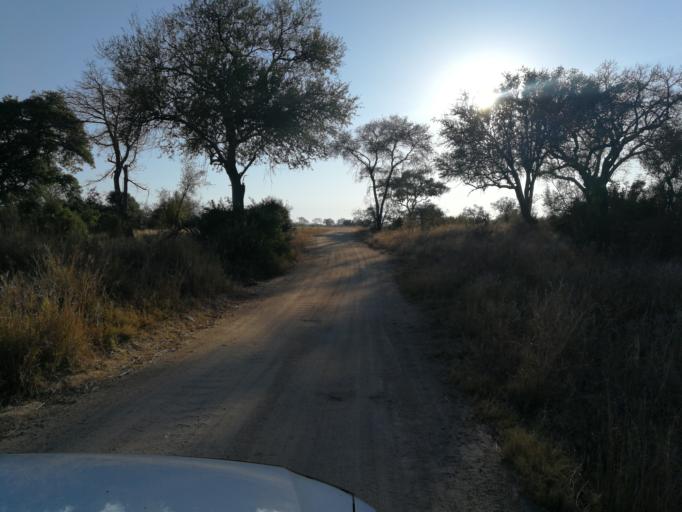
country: ZA
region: Limpopo
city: Thulamahashi
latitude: -25.0111
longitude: 31.4309
